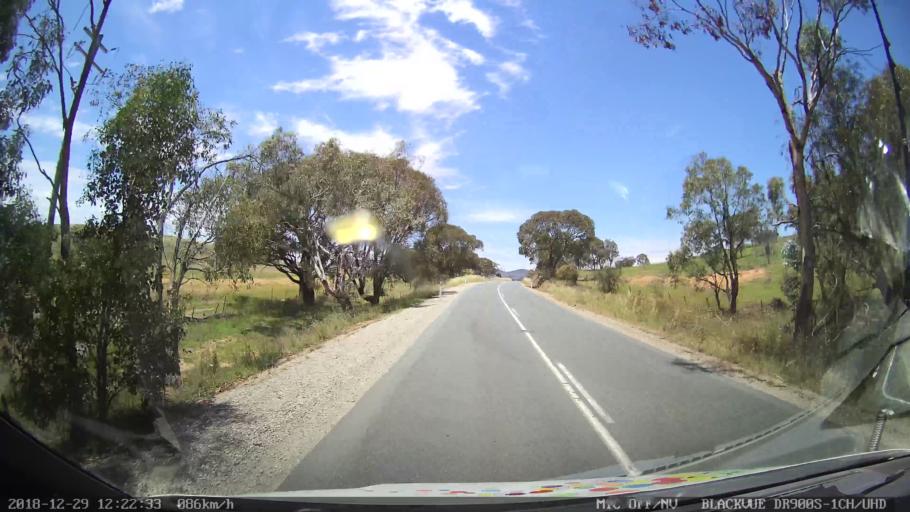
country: AU
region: New South Wales
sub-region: Queanbeyan
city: Queanbeyan
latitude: -35.4262
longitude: 149.2202
